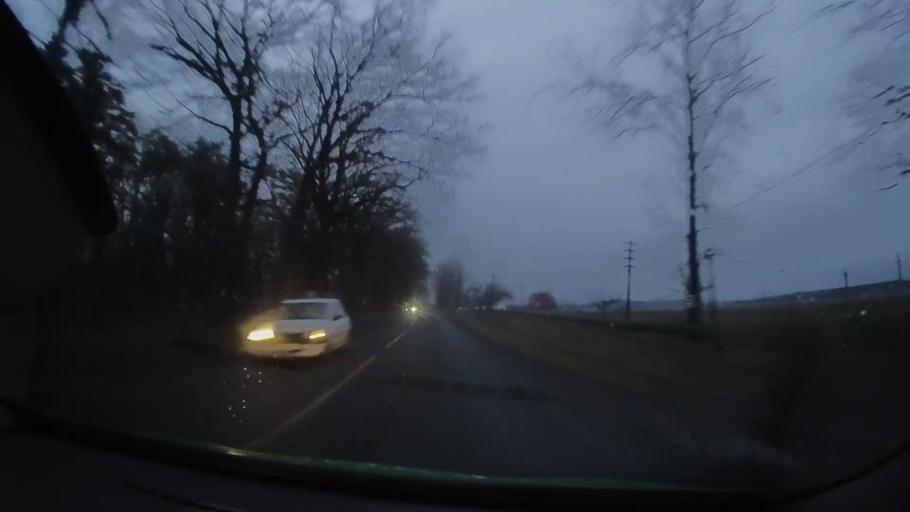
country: RO
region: Mures
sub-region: Comuna Solovastru
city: Solovastru
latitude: 46.7695
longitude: 24.7477
